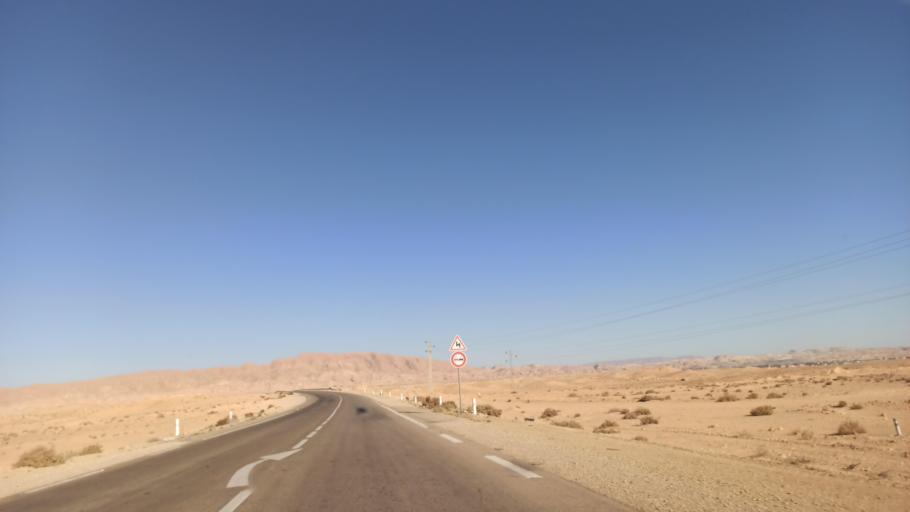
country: TN
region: Gafsa
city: Al Metlaoui
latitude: 34.2894
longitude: 8.3532
